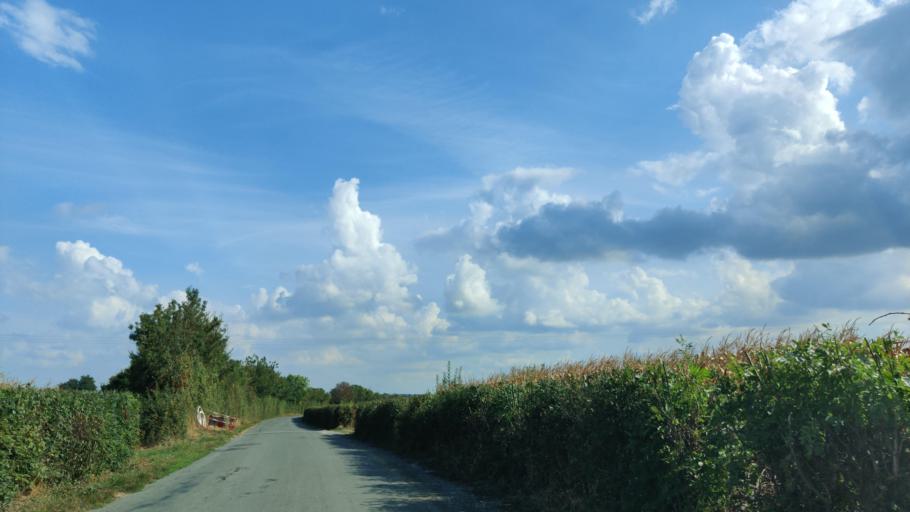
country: FR
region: Poitou-Charentes
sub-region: Departement des Deux-Sevres
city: Bessines
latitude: 46.2937
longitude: -0.5124
